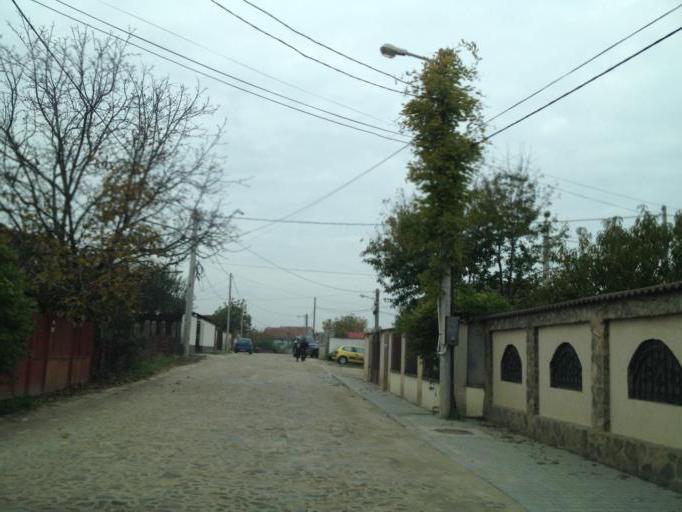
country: RO
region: Dolj
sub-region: Municipiul Craiova
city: Facai
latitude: 44.2923
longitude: 23.8095
